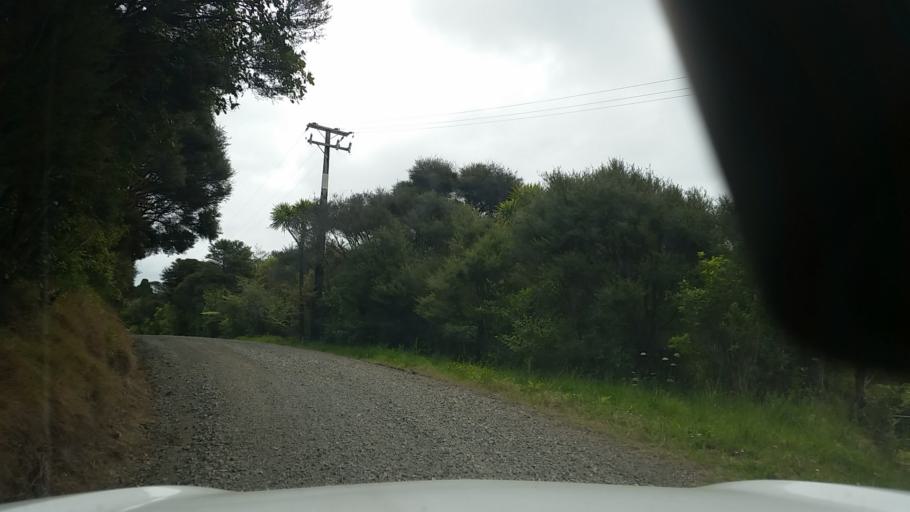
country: NZ
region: Auckland
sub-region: Auckland
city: Muriwai Beach
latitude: -36.8717
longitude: 174.5153
